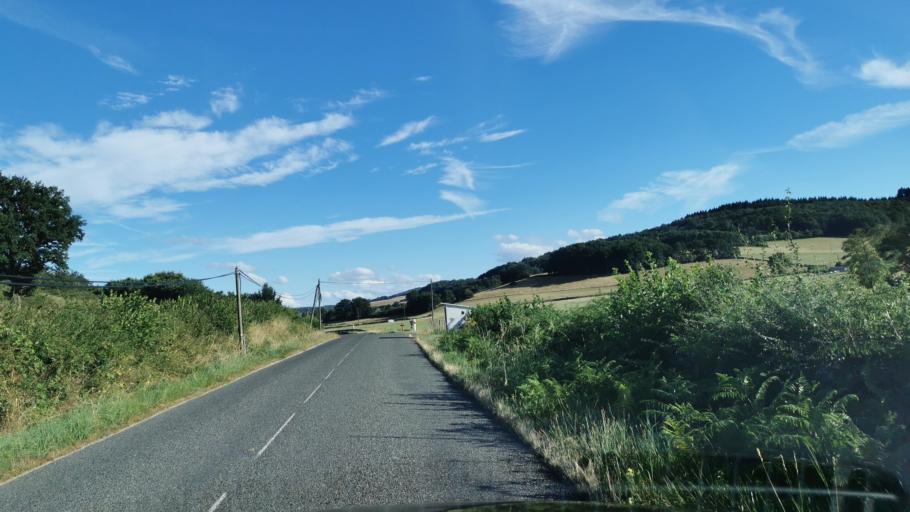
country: FR
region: Bourgogne
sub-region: Departement de Saone-et-Loire
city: Marmagne
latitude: 46.8295
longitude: 4.3180
